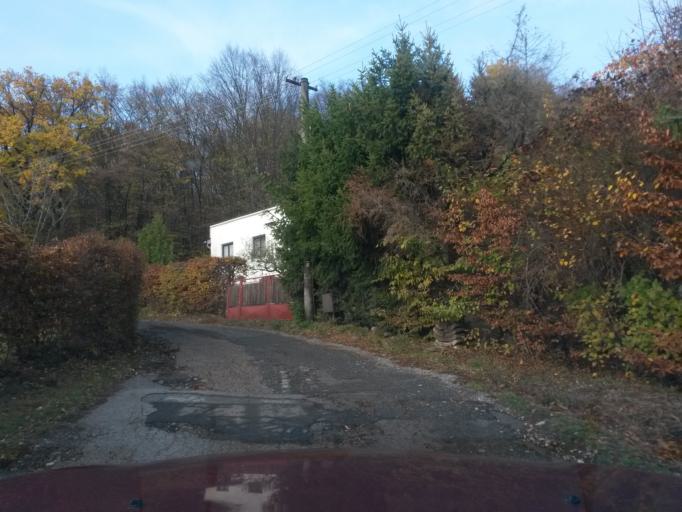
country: SK
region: Kosicky
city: Kosice
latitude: 48.7547
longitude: 21.2241
